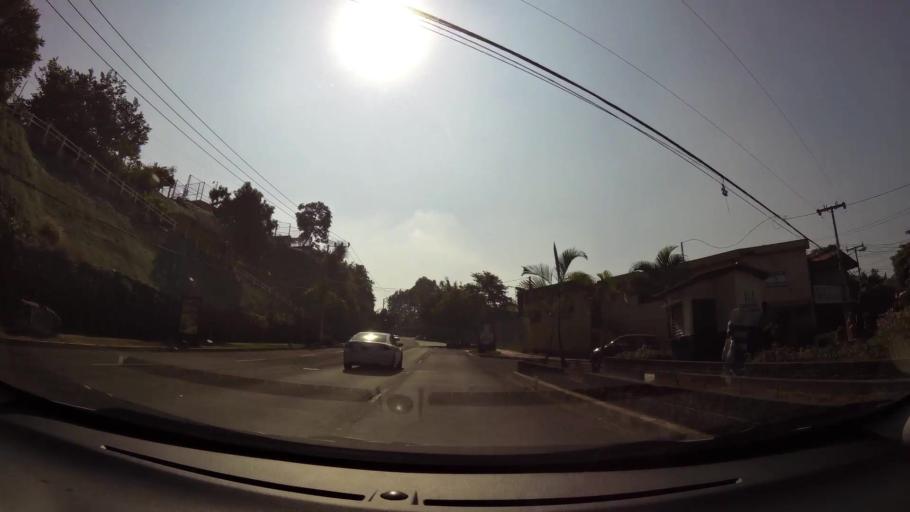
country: SV
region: La Libertad
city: Antiguo Cuscatlan
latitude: 13.6709
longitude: -89.2381
